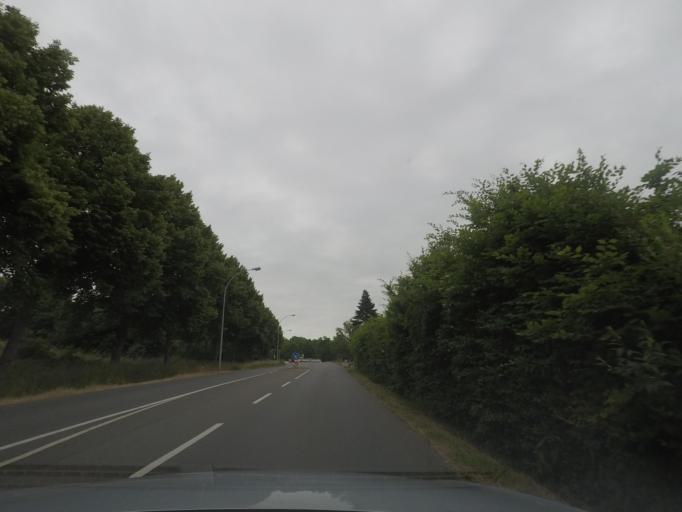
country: DE
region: Lower Saxony
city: Helmstedt
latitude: 52.2404
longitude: 11.0086
